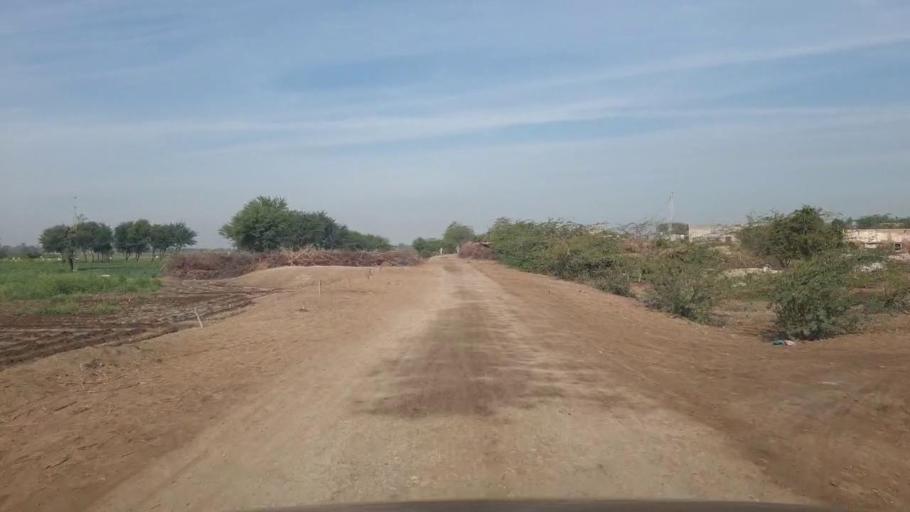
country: PK
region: Sindh
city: Umarkot
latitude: 25.3551
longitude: 69.6764
